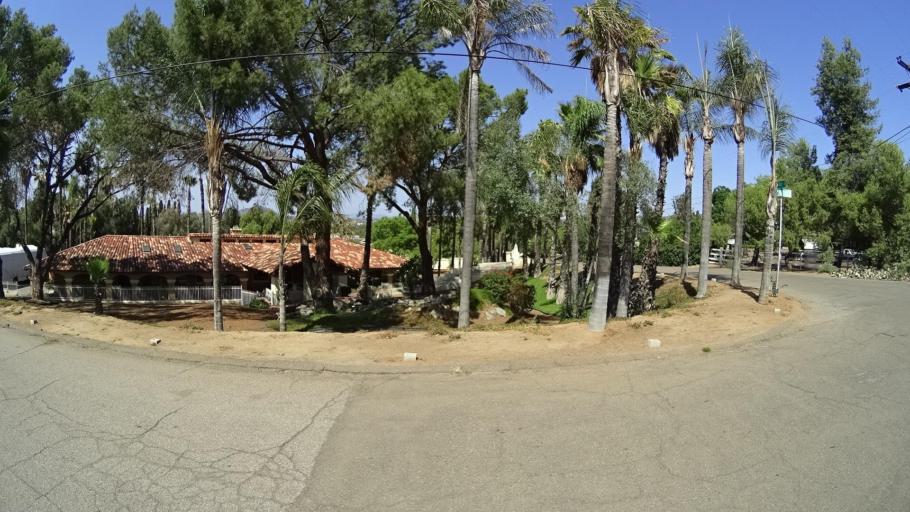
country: US
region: California
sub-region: San Diego County
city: Granite Hills
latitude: 32.7830
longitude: -116.9175
